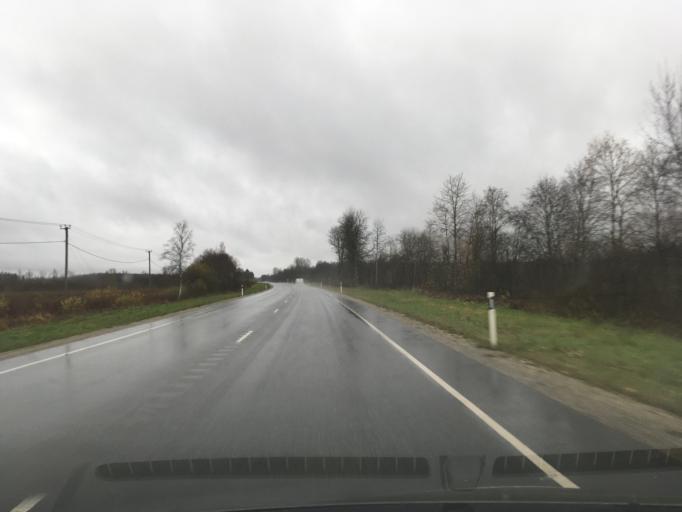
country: EE
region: Laeaene
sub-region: Lihula vald
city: Lihula
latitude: 58.8117
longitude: 24.0514
